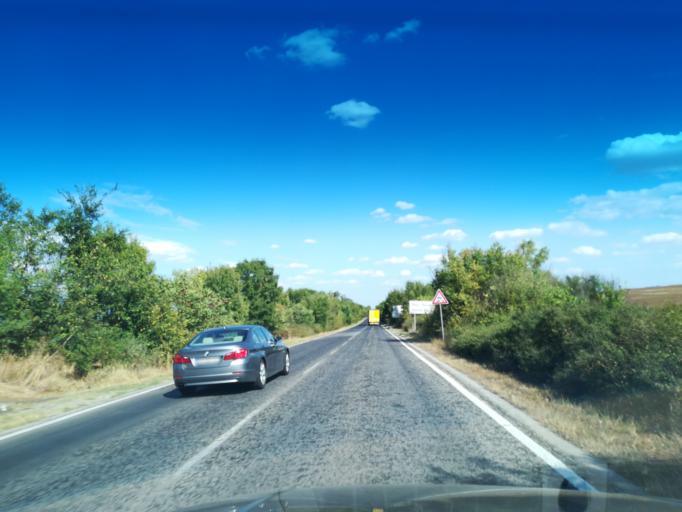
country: BG
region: Khaskovo
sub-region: Obshtina Mineralni Bani
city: Mineralni Bani
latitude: 42.0550
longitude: 25.3064
